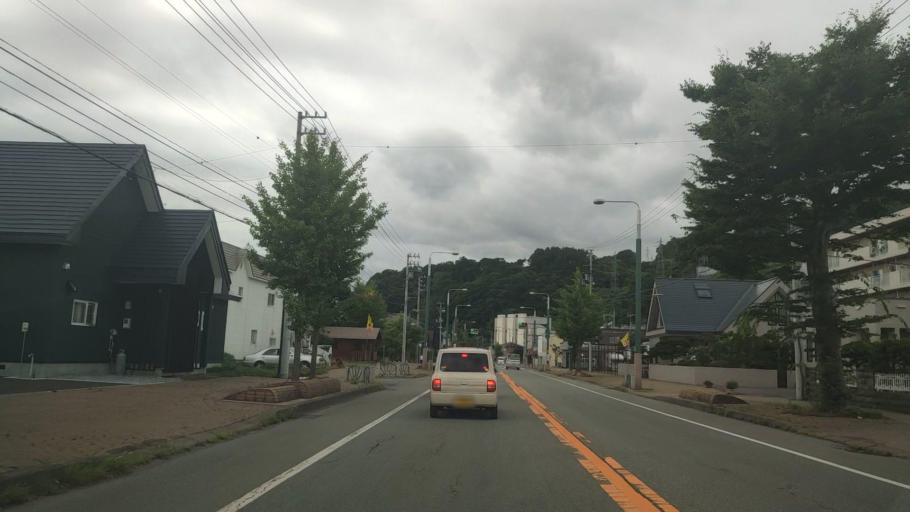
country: JP
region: Hokkaido
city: Date
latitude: 42.5514
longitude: 140.7618
